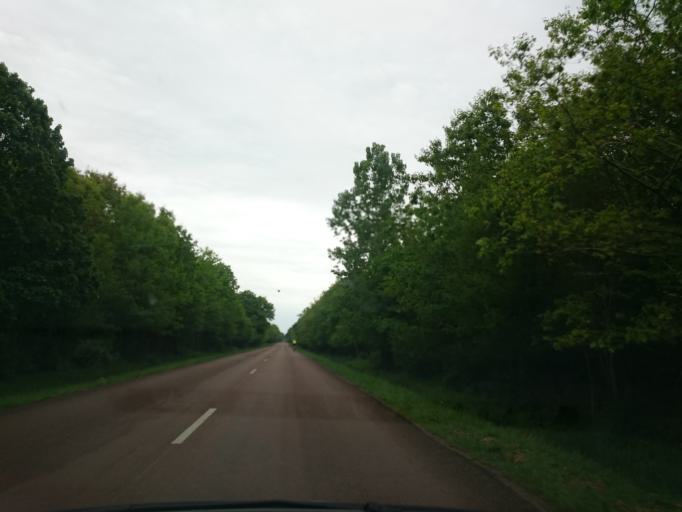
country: FR
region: Centre
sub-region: Departement du Loir-et-Cher
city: Muides-sur-Loire
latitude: 47.6537
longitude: 1.5320
